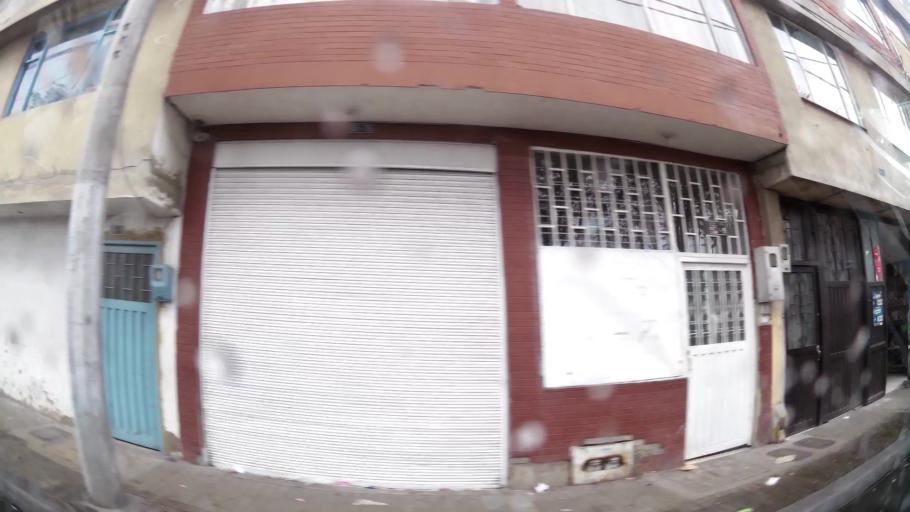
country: CO
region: Bogota D.C.
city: Bogota
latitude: 4.6598
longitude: -74.1010
